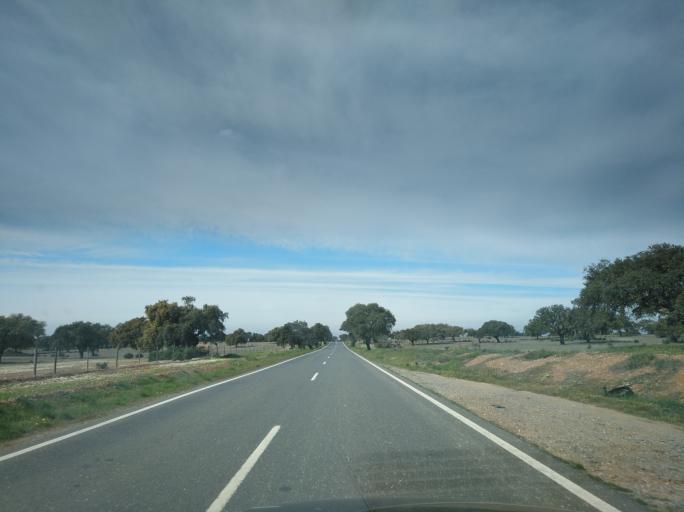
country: PT
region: Beja
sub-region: Mertola
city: Mertola
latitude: 37.7543
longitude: -7.8078
